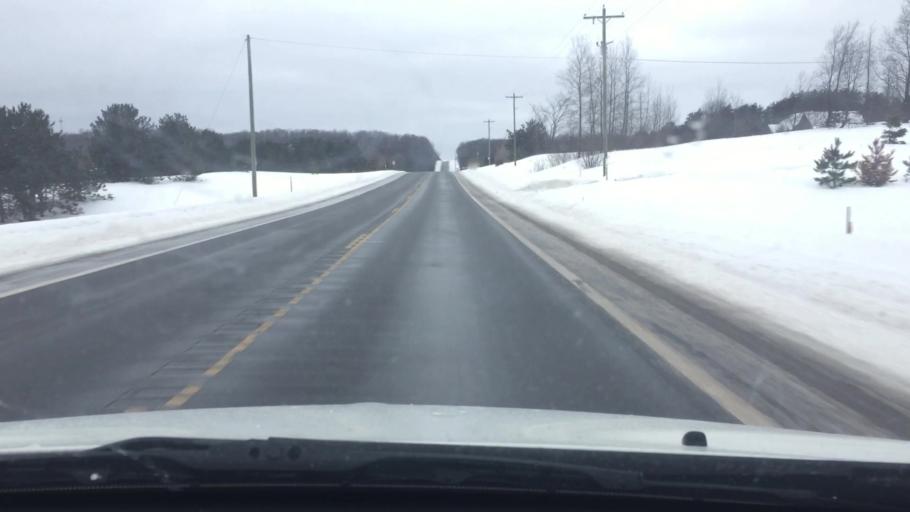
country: US
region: Michigan
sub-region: Charlevoix County
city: Boyne City
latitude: 45.0964
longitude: -84.9943
